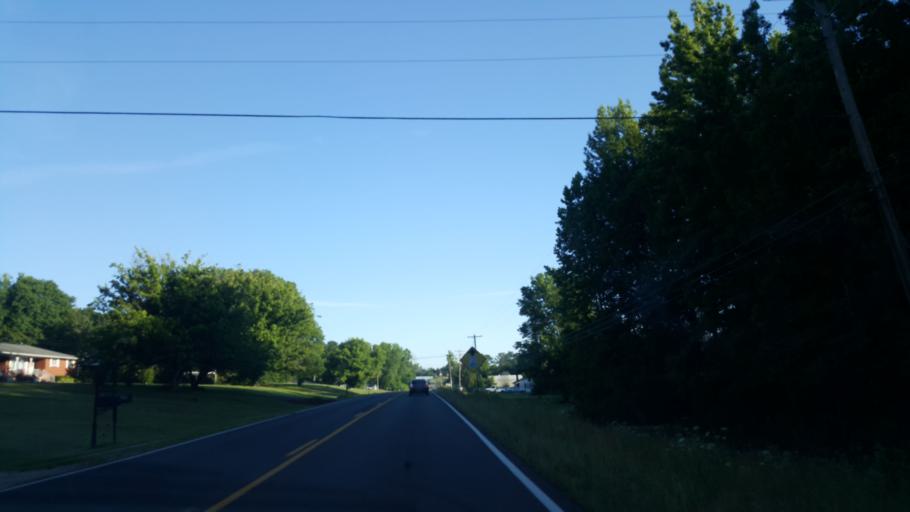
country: US
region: Tennessee
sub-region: Henderson County
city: Lexington
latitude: 35.6167
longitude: -88.4023
